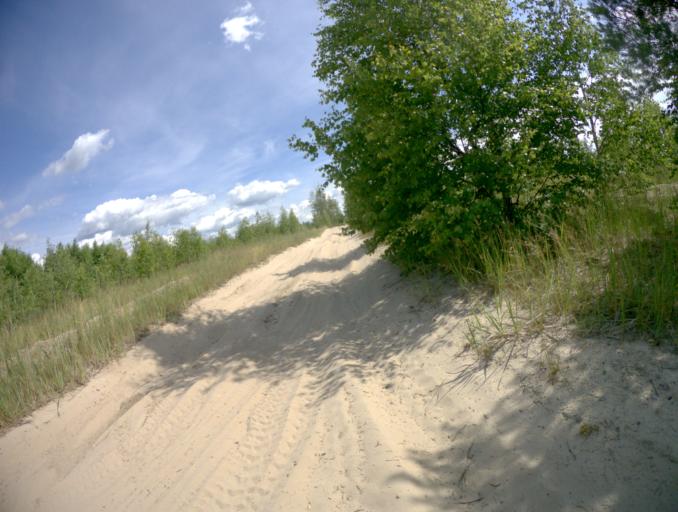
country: RU
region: Nizjnij Novgorod
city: Frolishchi
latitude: 56.4785
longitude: 42.5920
